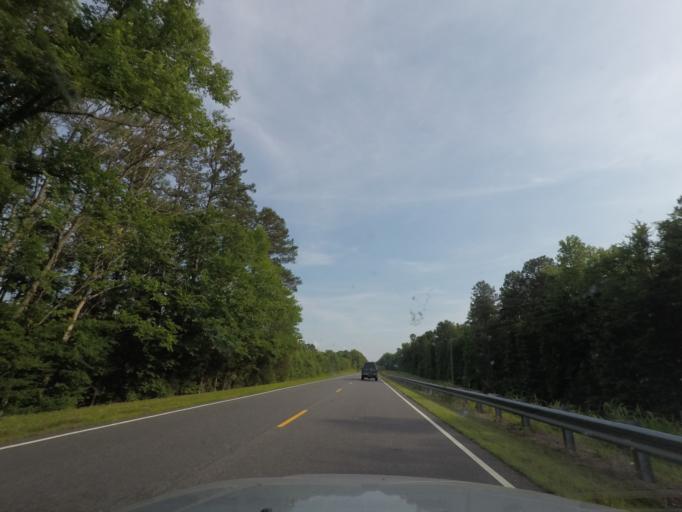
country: US
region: Virginia
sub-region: Mecklenburg County
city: Clarksville
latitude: 36.7176
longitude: -78.6308
